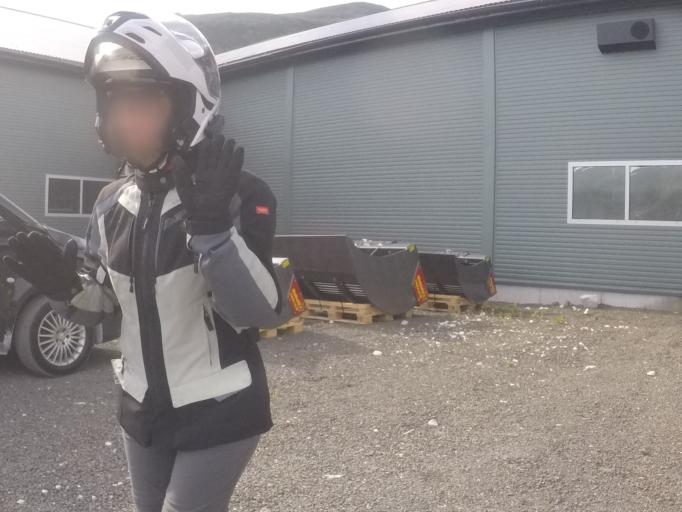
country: NO
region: More og Romsdal
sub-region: Eide
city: Eide
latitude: 62.8927
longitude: 7.3664
